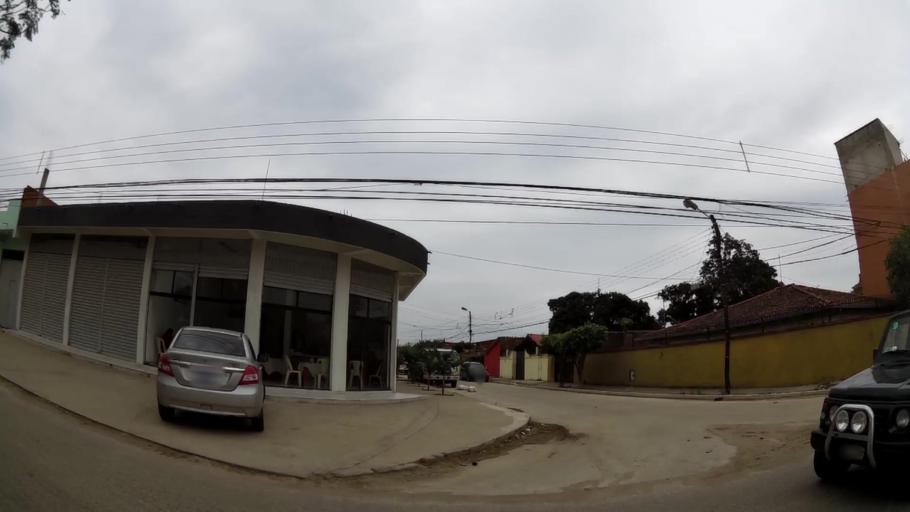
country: BO
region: Santa Cruz
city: Santa Cruz de la Sierra
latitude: -17.8205
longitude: -63.2097
